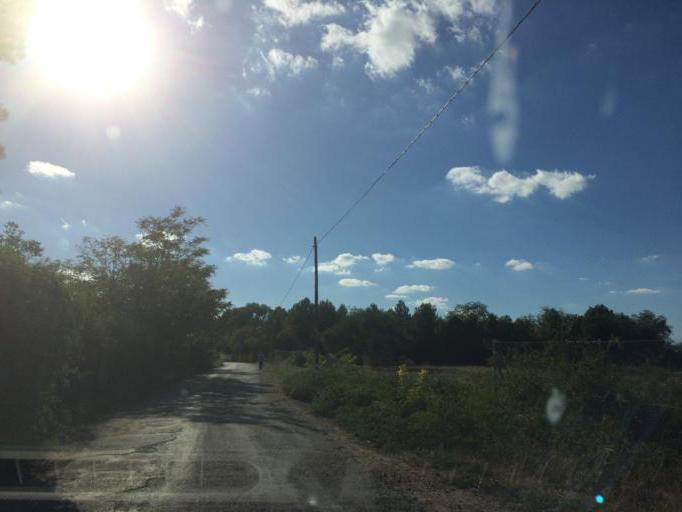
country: ES
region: Castille-La Mancha
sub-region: Provincia de Albacete
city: Albacete
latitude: 38.9940
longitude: -1.8797
